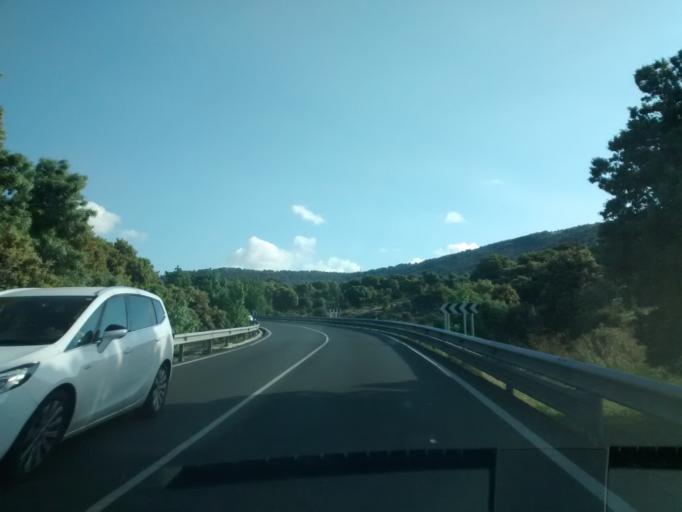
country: ES
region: Madrid
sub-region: Provincia de Madrid
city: Alpedrete
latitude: 40.6738
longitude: -4.0103
